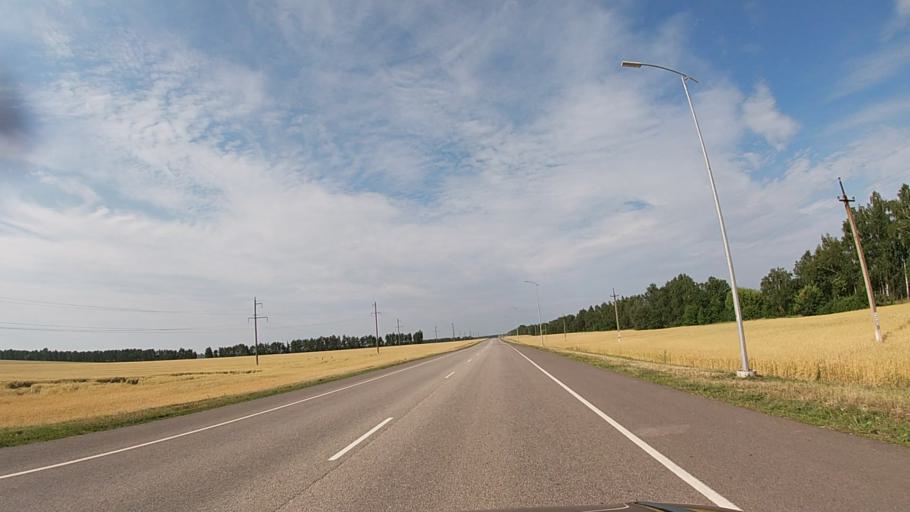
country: RU
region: Belgorod
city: Proletarskiy
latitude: 50.8257
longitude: 35.7604
